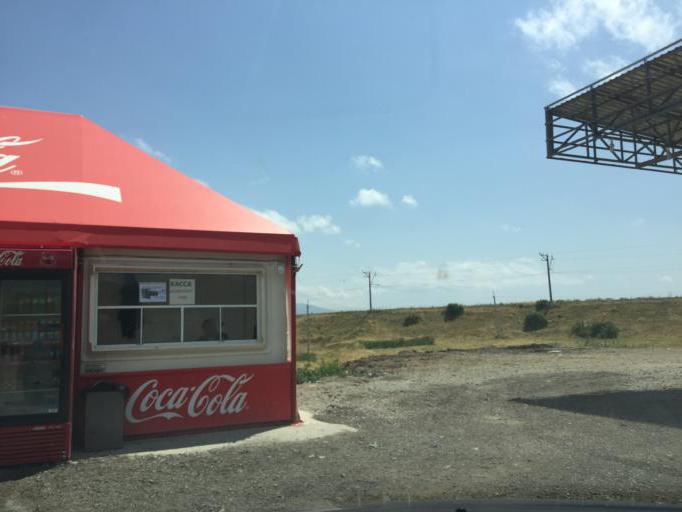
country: AM
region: Geghark'unik'i Marz
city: Tsovagyugh
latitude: 40.6174
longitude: 44.9525
